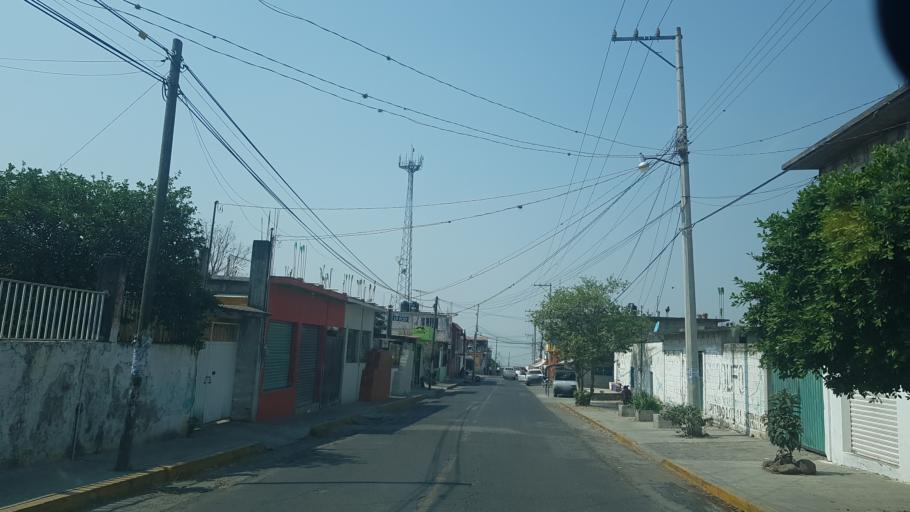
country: MX
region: Morelos
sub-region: Temoac
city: Temoac
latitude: 18.7752
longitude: -98.7768
